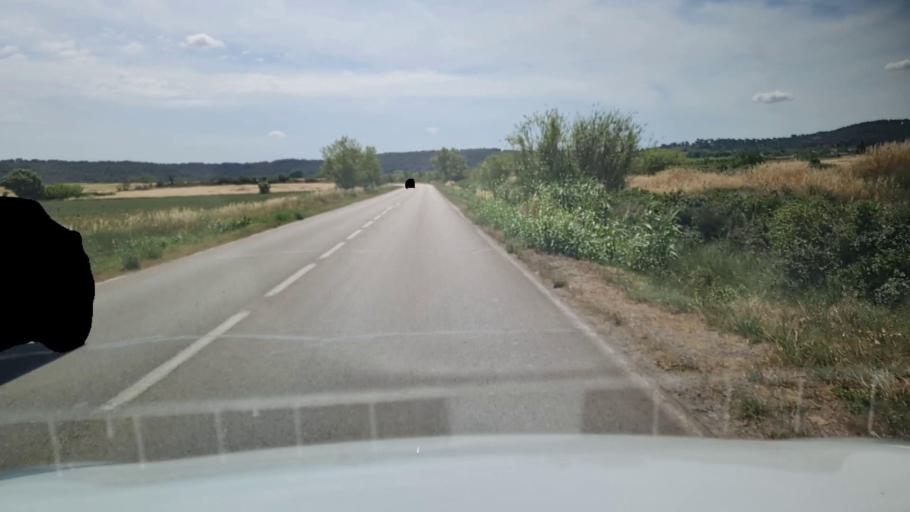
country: FR
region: Languedoc-Roussillon
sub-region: Departement du Gard
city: Clarensac
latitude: 43.8174
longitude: 4.2347
